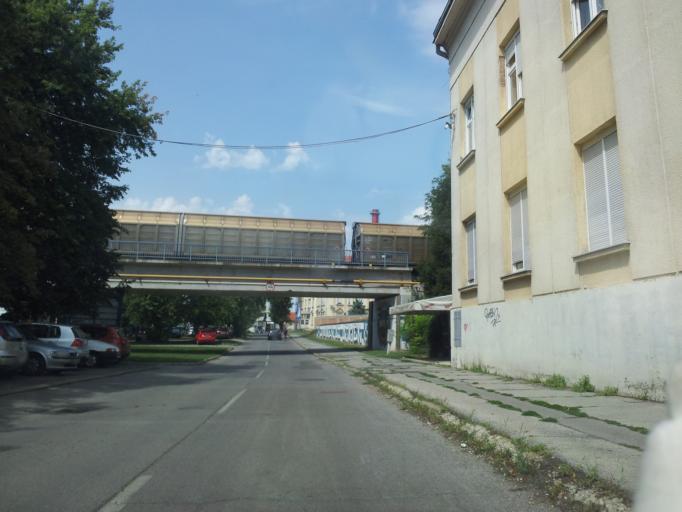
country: HR
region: Osjecko-Baranjska
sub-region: Grad Osijek
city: Osijek
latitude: 45.5591
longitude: 18.7045
